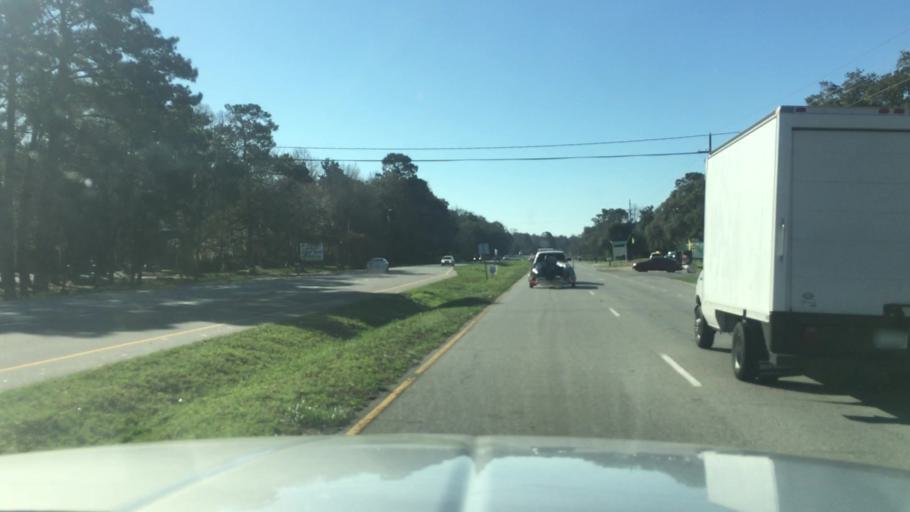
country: US
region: North Carolina
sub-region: New Hanover County
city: Sea Breeze
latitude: 34.0848
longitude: -77.8957
